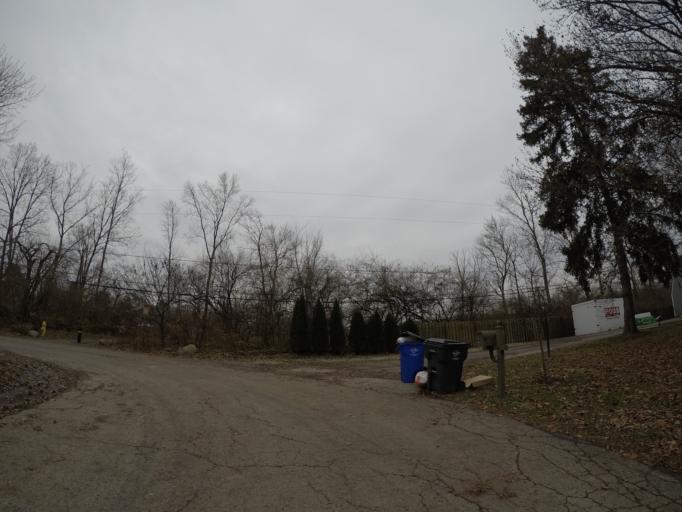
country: US
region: Ohio
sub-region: Franklin County
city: Dublin
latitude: 40.0576
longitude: -83.0829
